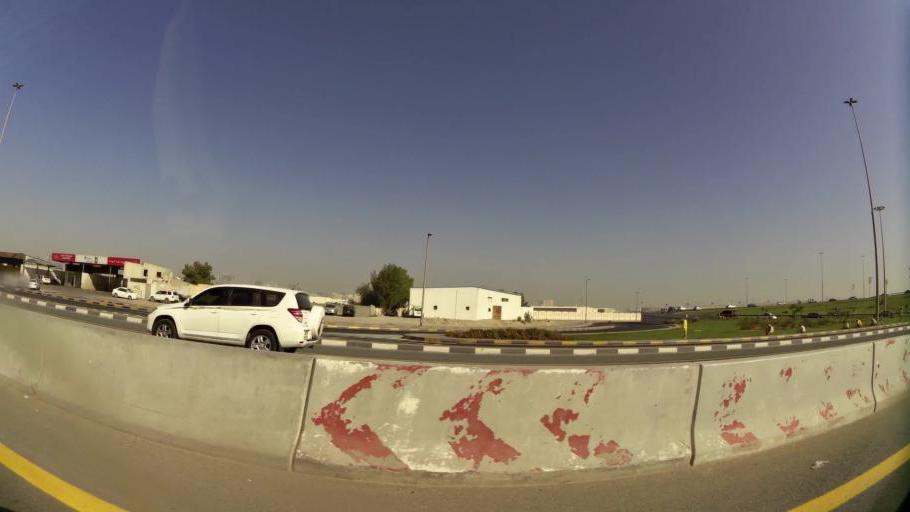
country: AE
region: Ash Shariqah
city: Sharjah
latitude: 25.3266
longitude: 55.4189
